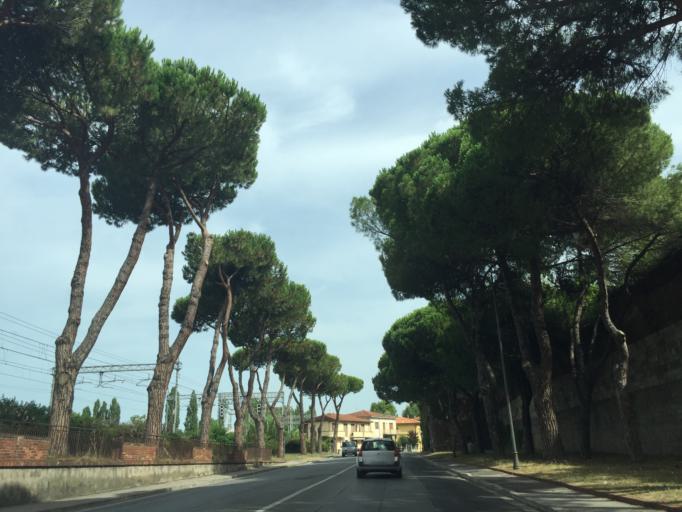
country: IT
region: Tuscany
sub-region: Province of Pisa
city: Pisa
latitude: 43.7145
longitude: 10.3883
